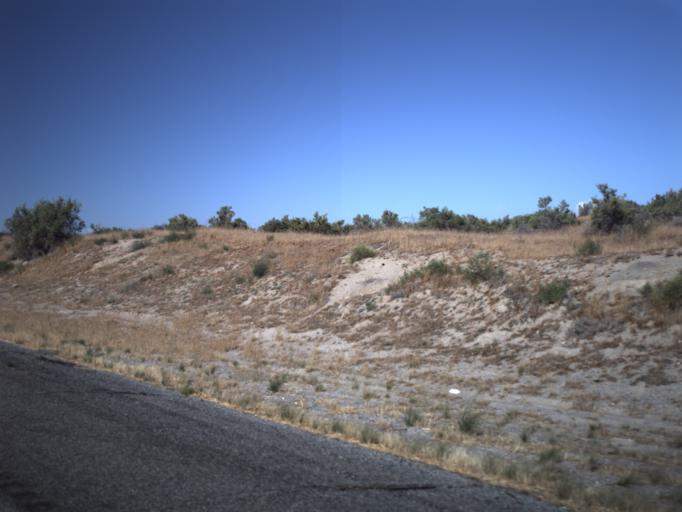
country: US
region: Utah
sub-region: Millard County
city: Delta
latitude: 39.4206
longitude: -112.4771
